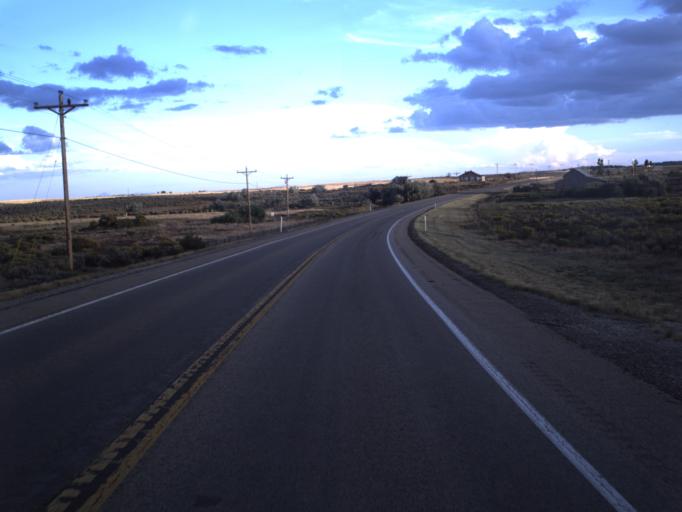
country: US
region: Utah
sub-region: San Juan County
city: Monticello
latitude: 37.9511
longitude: -109.3470
